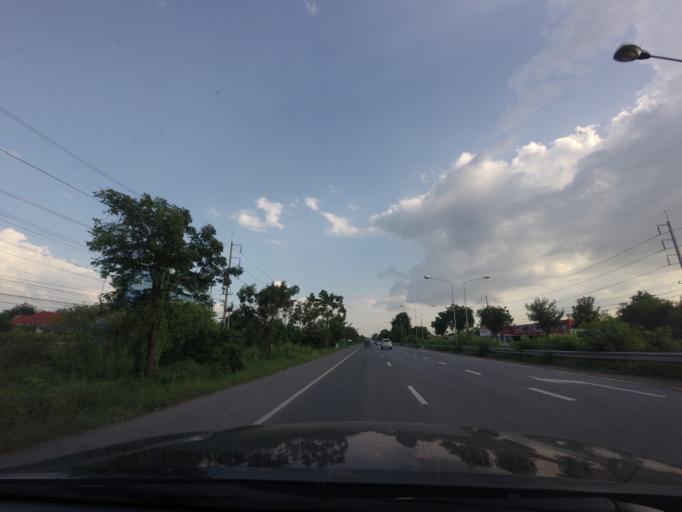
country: TH
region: Sara Buri
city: Saraburi
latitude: 14.5309
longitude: 100.8865
